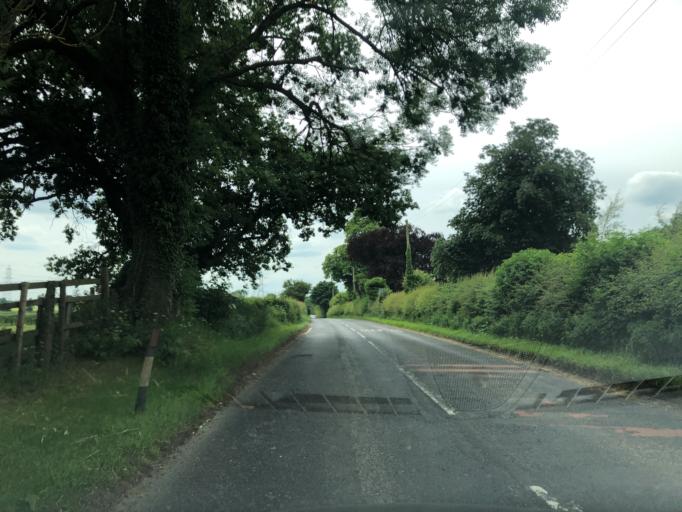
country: GB
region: England
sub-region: North Yorkshire
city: Angram Grange
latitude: 54.2363
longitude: -1.2648
